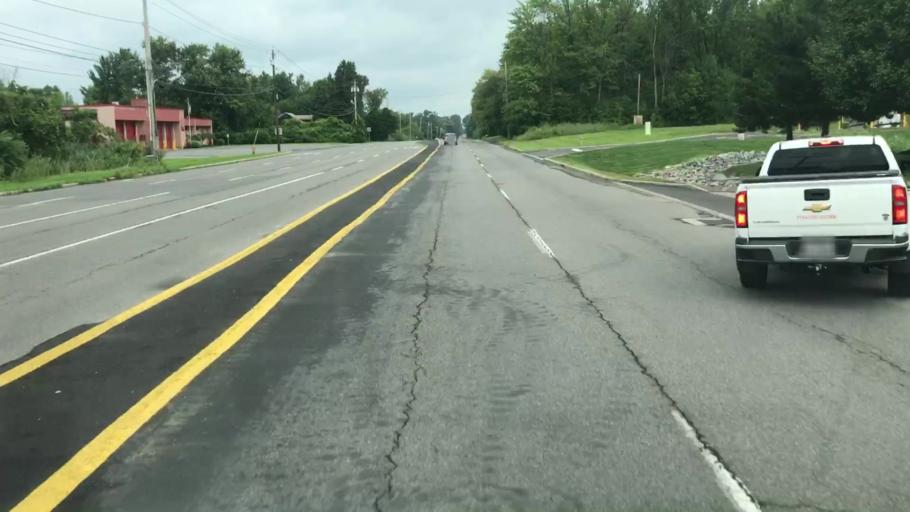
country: US
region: New York
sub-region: Onondaga County
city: Liverpool
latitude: 43.1417
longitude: -76.2067
